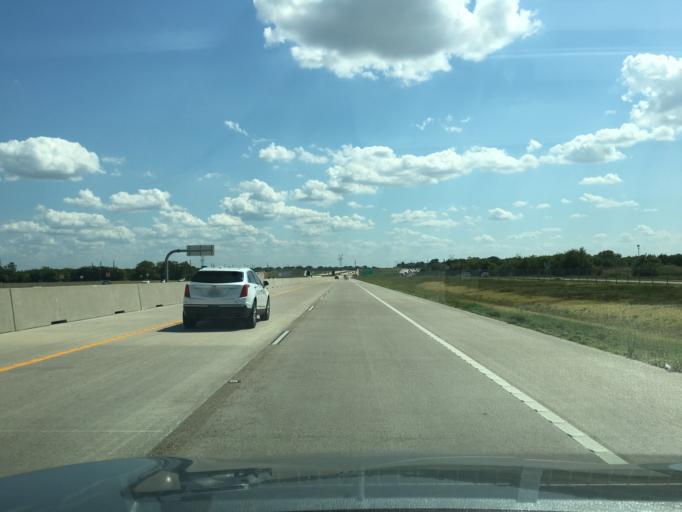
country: US
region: Texas
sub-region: Tarrant County
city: Arlington
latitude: 32.6426
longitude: -97.0632
